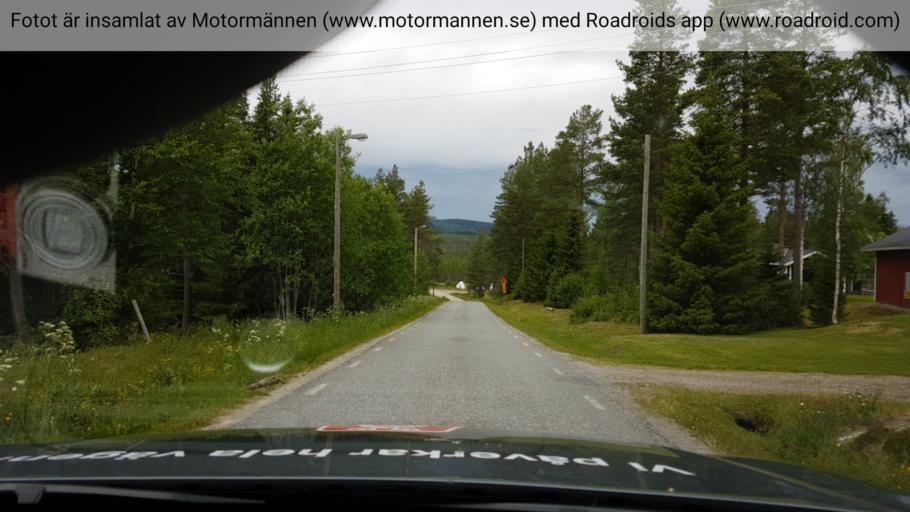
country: SE
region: Jaemtland
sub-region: Bergs Kommun
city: Hoverberg
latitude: 62.5649
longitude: 14.3771
